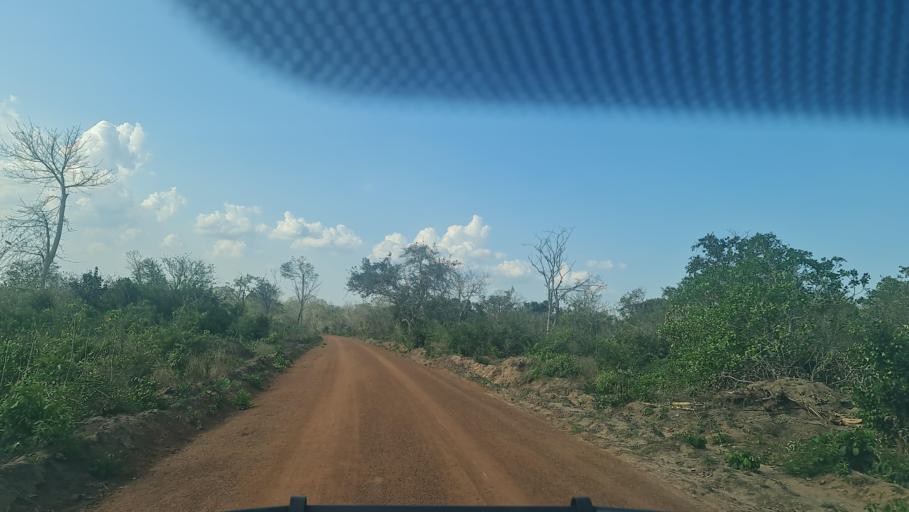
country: MZ
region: Nampula
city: Ilha de Mocambique
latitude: -15.5086
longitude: 40.1637
